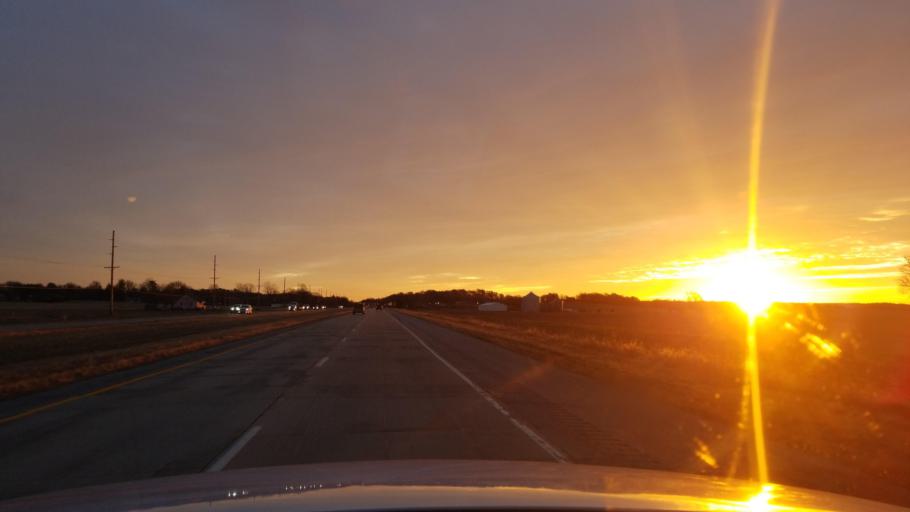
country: US
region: Indiana
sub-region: Posey County
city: Mount Vernon
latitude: 37.9419
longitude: -87.7632
